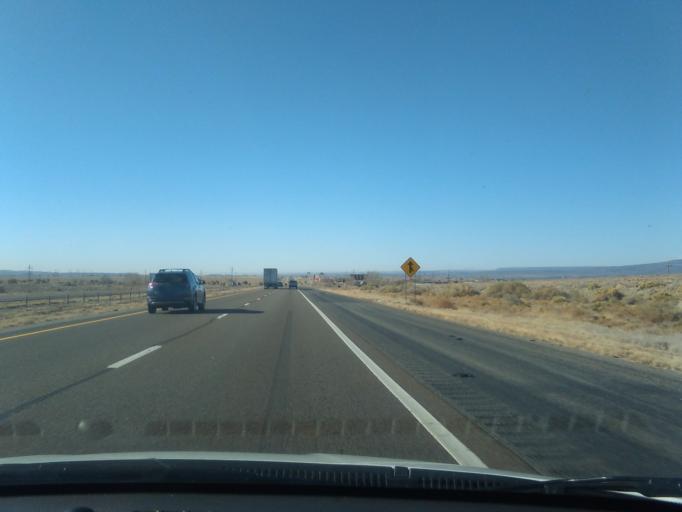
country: US
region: New Mexico
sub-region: Sandoval County
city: Santo Domingo Pueblo
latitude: 35.4589
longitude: -106.3324
